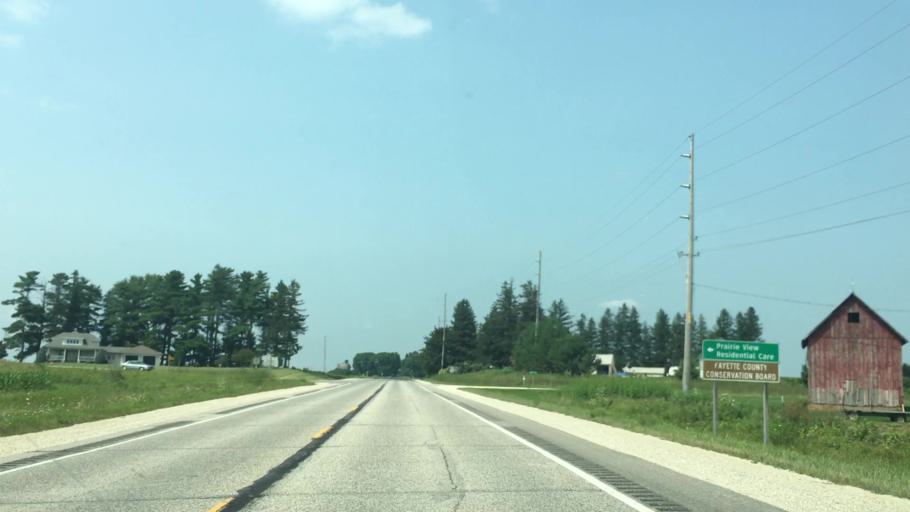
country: US
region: Iowa
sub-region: Fayette County
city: West Union
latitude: 42.9053
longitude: -91.8114
